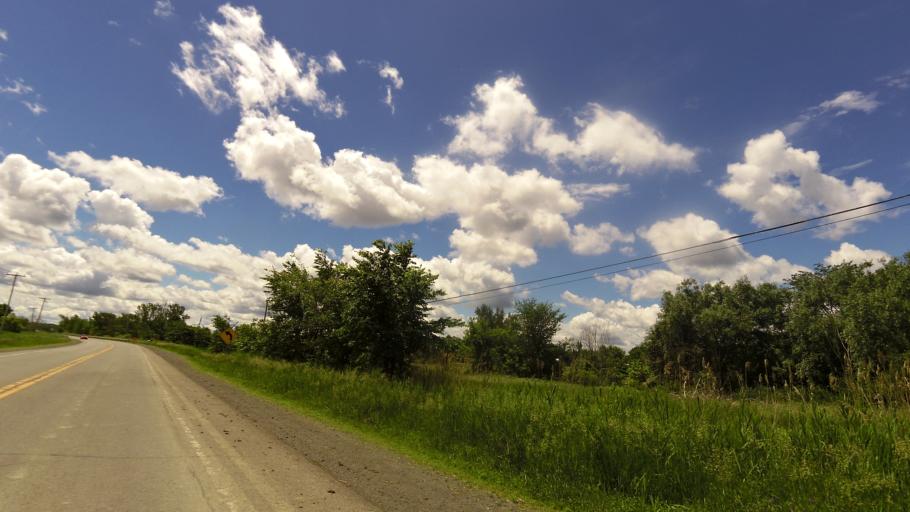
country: CA
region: Quebec
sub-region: Monteregie
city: Hudson
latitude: 45.5203
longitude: -74.1676
